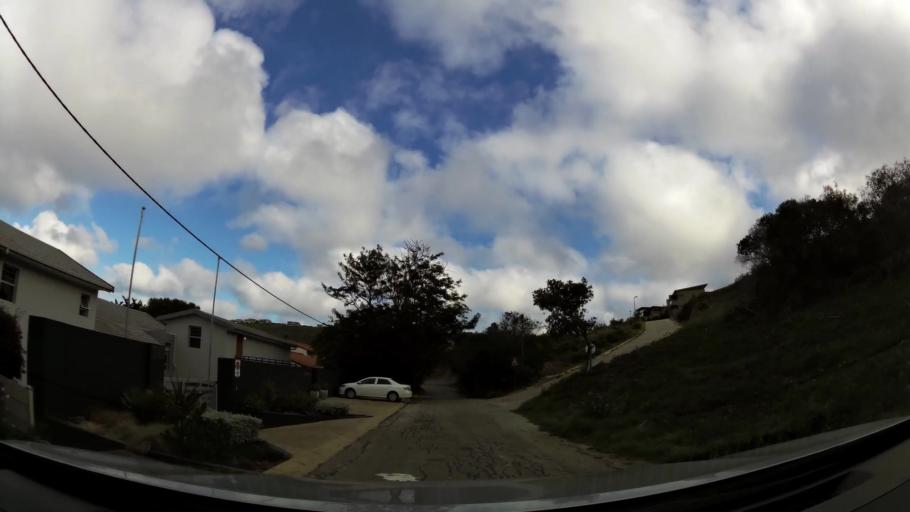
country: ZA
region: Western Cape
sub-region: Eden District Municipality
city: Plettenberg Bay
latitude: -34.0832
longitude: 23.3607
